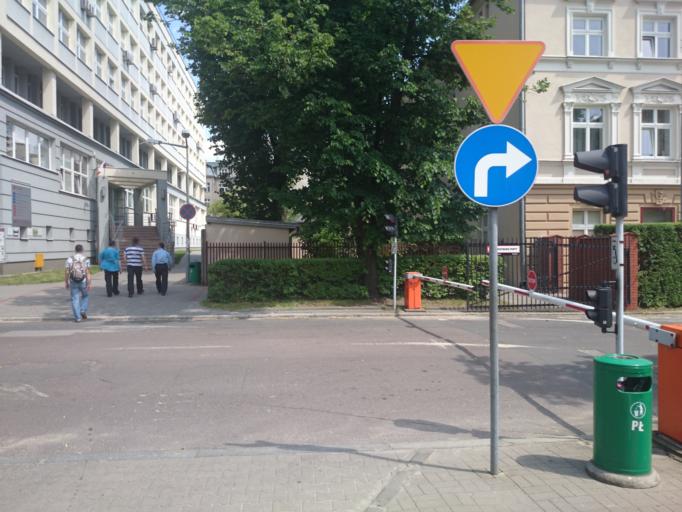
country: PL
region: Lodz Voivodeship
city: Lodz
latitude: 51.7524
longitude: 19.4527
